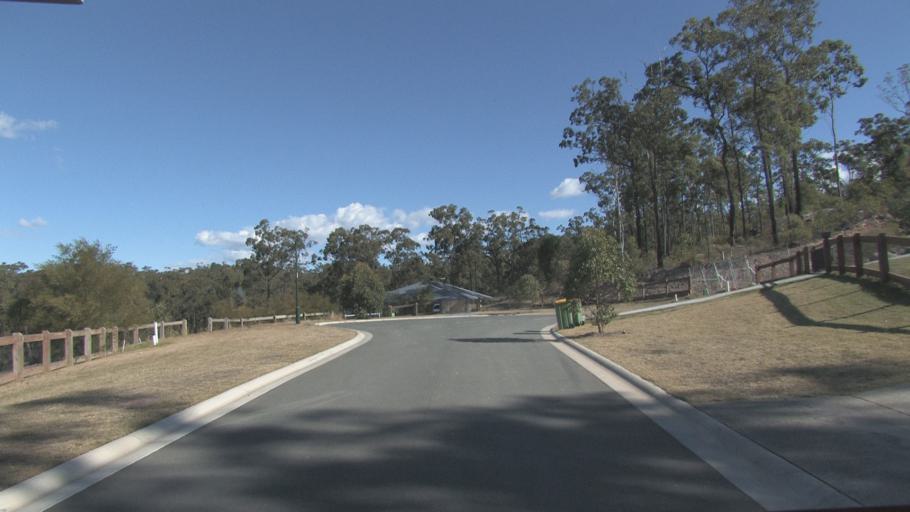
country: AU
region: Queensland
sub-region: Ipswich
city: Springfield Lakes
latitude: -27.7336
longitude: 152.9044
